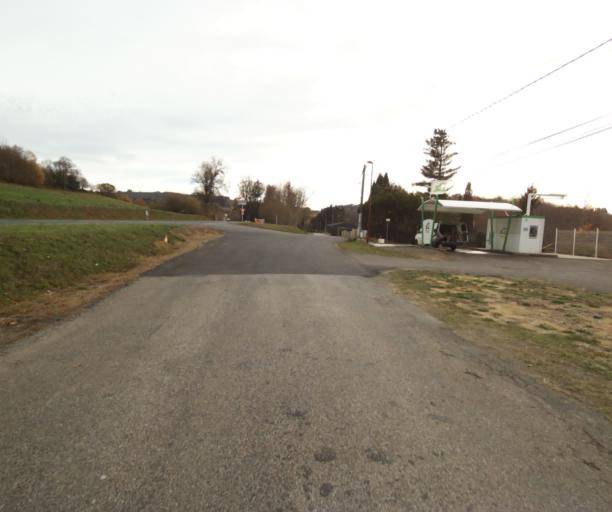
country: FR
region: Limousin
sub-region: Departement de la Correze
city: Sainte-Fortunade
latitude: 45.2206
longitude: 1.7672
